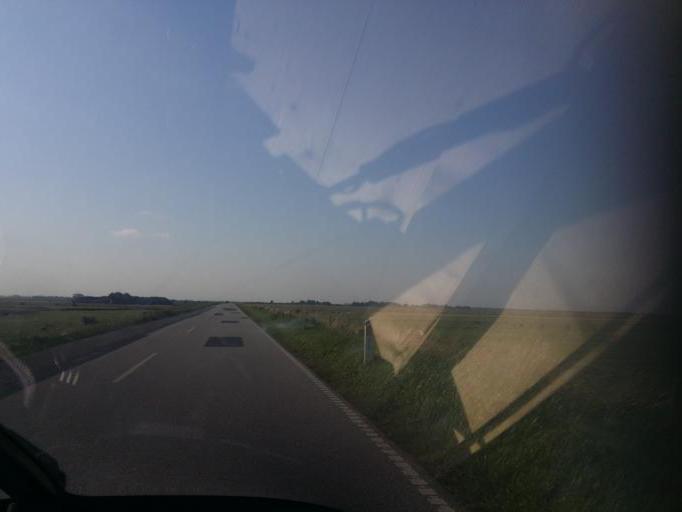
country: DE
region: Schleswig-Holstein
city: Rodenas
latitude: 54.9428
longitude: 8.7098
